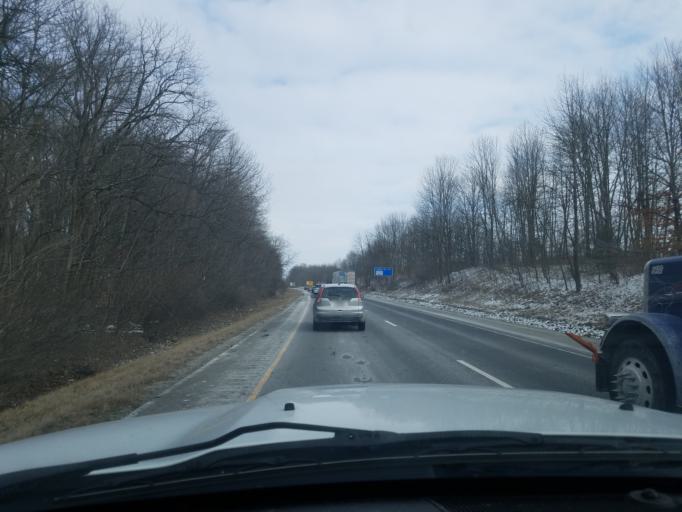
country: US
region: Indiana
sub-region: Henry County
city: New Castle
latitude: 39.8527
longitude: -85.4391
